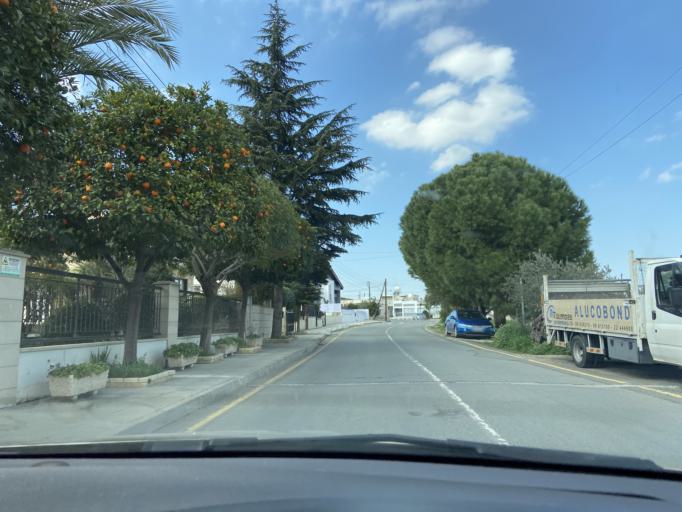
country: CY
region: Lefkosia
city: Alampra
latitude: 35.0190
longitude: 33.3903
